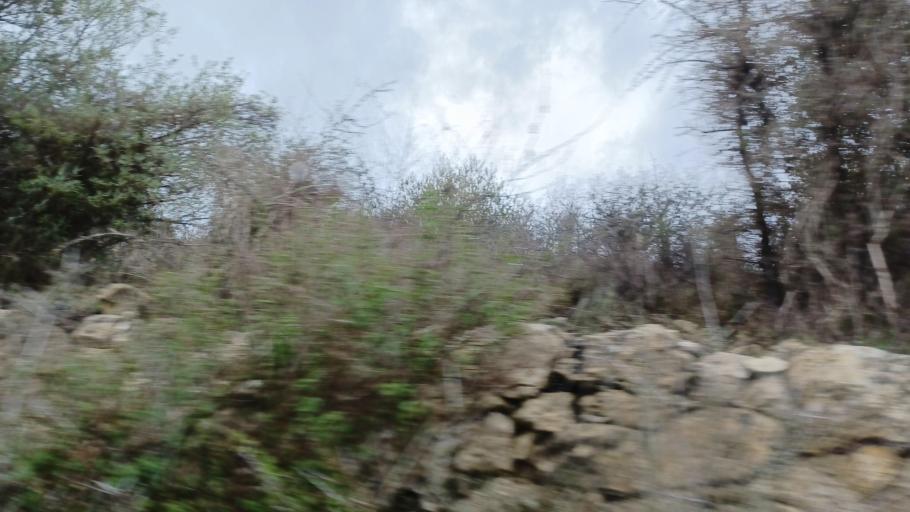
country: CY
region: Limassol
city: Pachna
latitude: 34.8273
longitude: 32.7317
